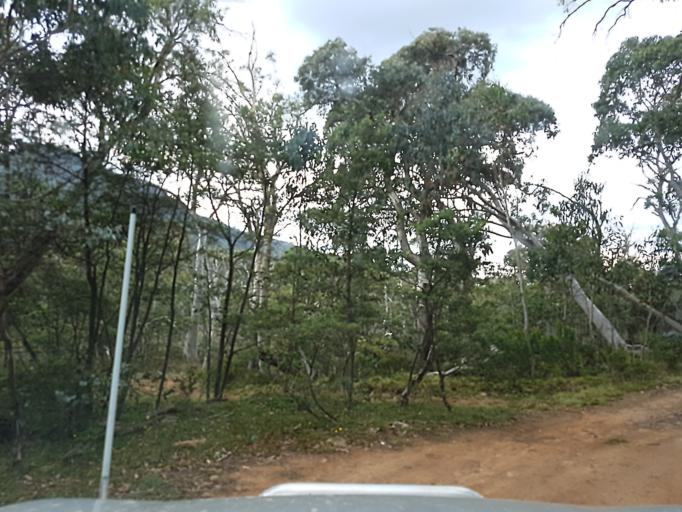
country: AU
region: New South Wales
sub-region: Snowy River
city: Jindabyne
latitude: -36.8807
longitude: 148.1596
